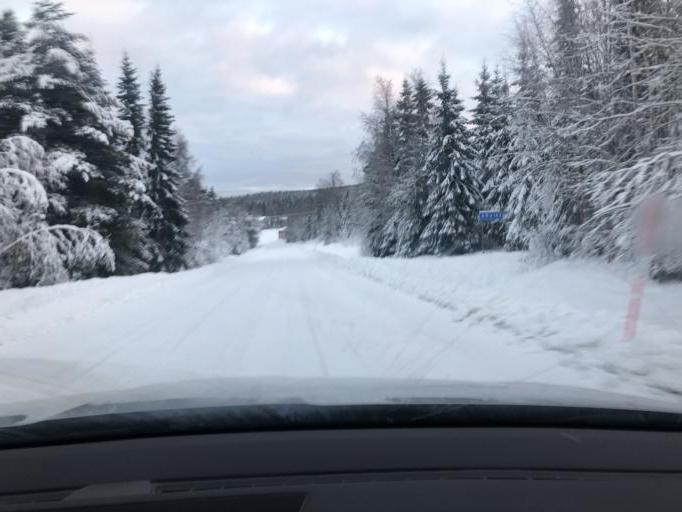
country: SE
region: Vaesternorrland
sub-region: Kramfors Kommun
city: Nordingra
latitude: 63.0001
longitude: 18.2184
